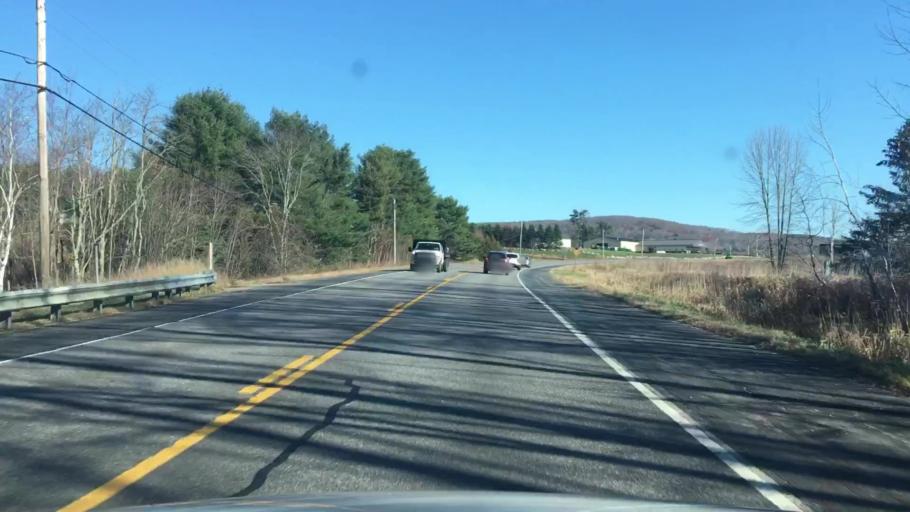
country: US
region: Maine
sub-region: Knox County
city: Union
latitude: 44.2173
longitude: -69.2917
